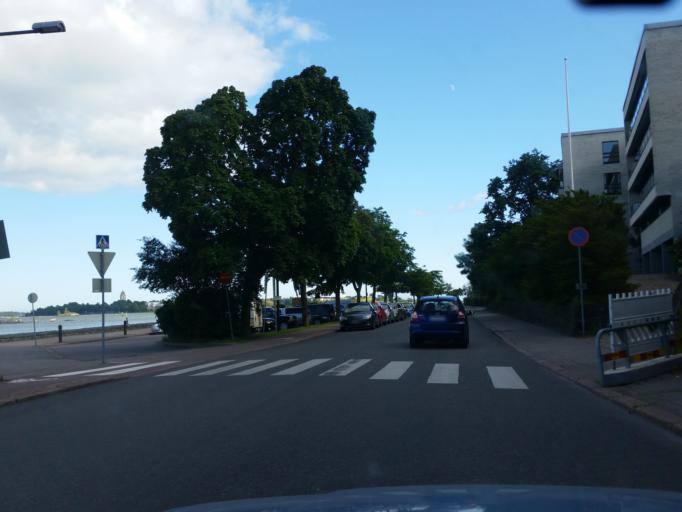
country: FI
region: Uusimaa
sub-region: Helsinki
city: Helsinki
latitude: 60.1596
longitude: 24.9609
